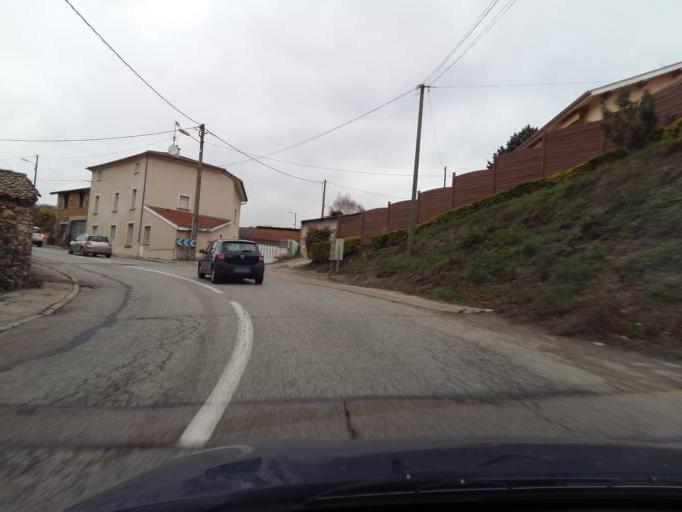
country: FR
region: Rhone-Alpes
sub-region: Departement de l'Ardeche
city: Andance
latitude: 45.2476
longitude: 4.7822
